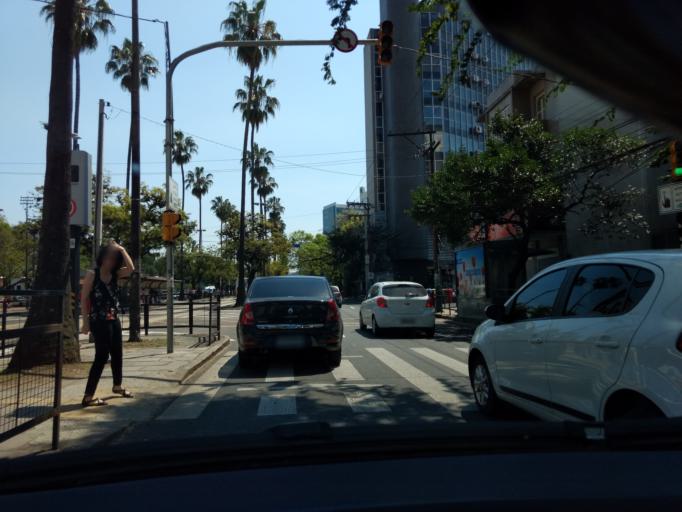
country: BR
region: Rio Grande do Sul
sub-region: Porto Alegre
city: Porto Alegre
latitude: -30.0365
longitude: -51.2094
